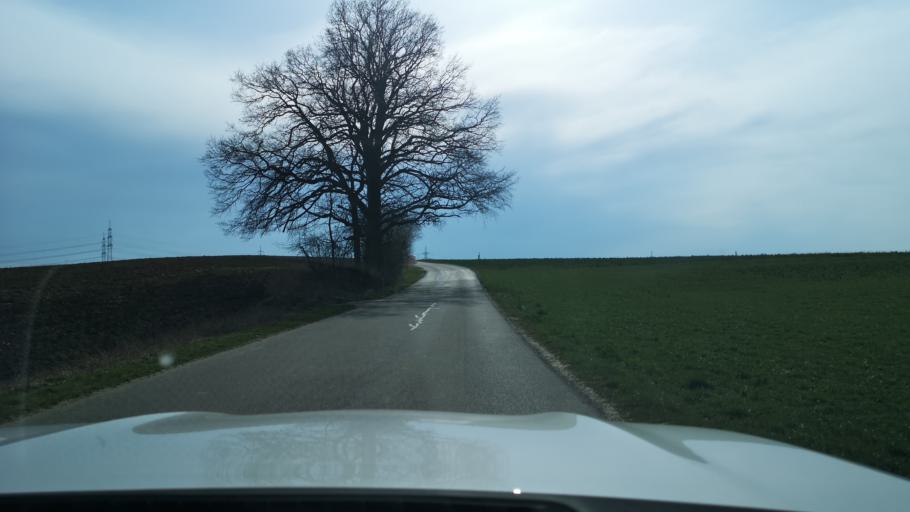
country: DE
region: Bavaria
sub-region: Upper Bavaria
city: Finsing
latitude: 48.2348
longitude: 11.8378
